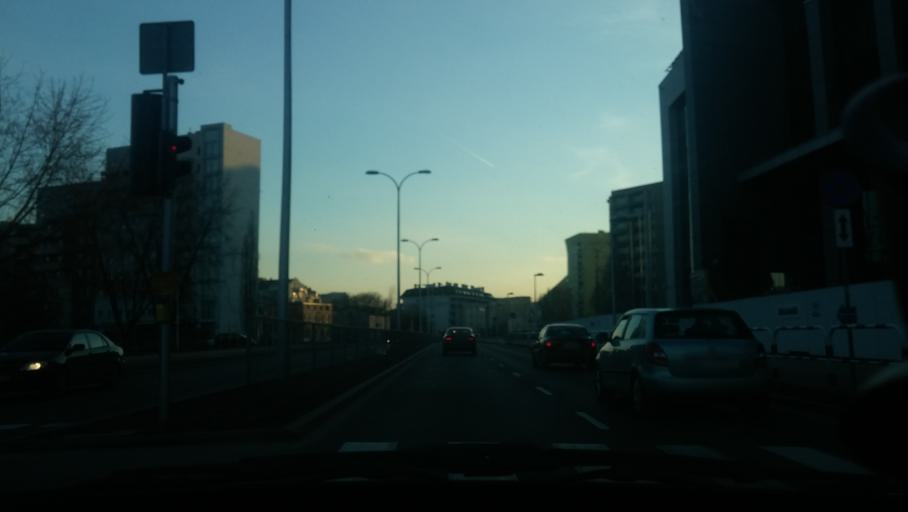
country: PL
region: Masovian Voivodeship
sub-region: Warszawa
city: Praga Poludnie
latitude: 52.2349
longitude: 21.0857
